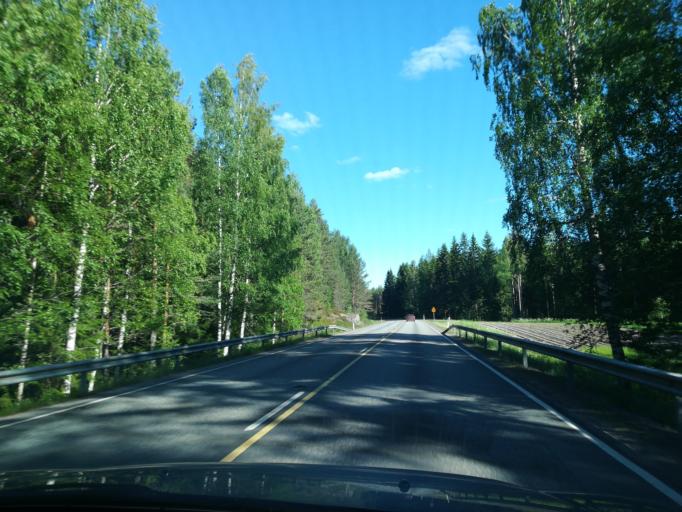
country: FI
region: South Karelia
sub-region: Imatra
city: Ruokolahti
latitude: 61.3678
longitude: 28.6798
